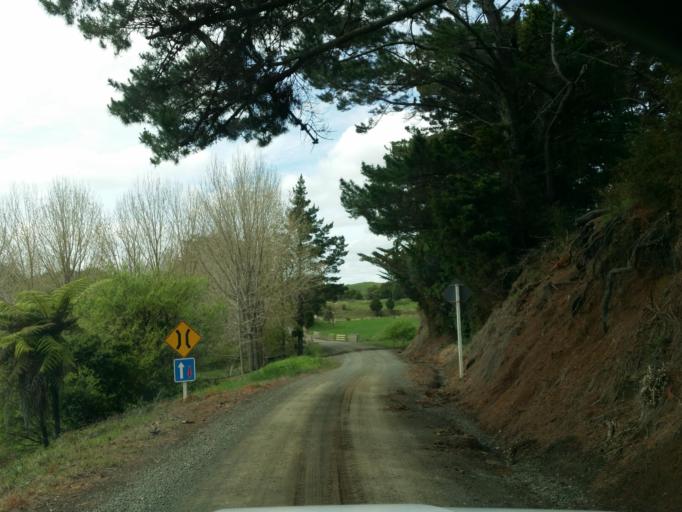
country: NZ
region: Northland
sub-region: Whangarei
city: Maungatapere
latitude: -35.9050
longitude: 174.1272
